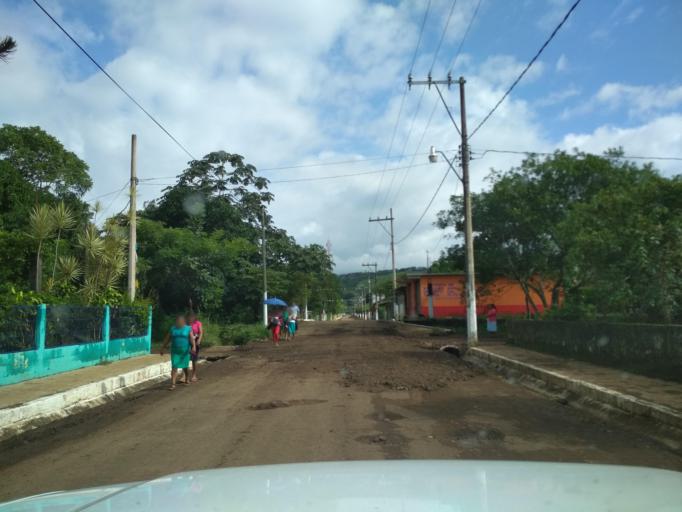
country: MX
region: Veracruz
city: Catemaco
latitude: 18.3757
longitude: -95.1237
